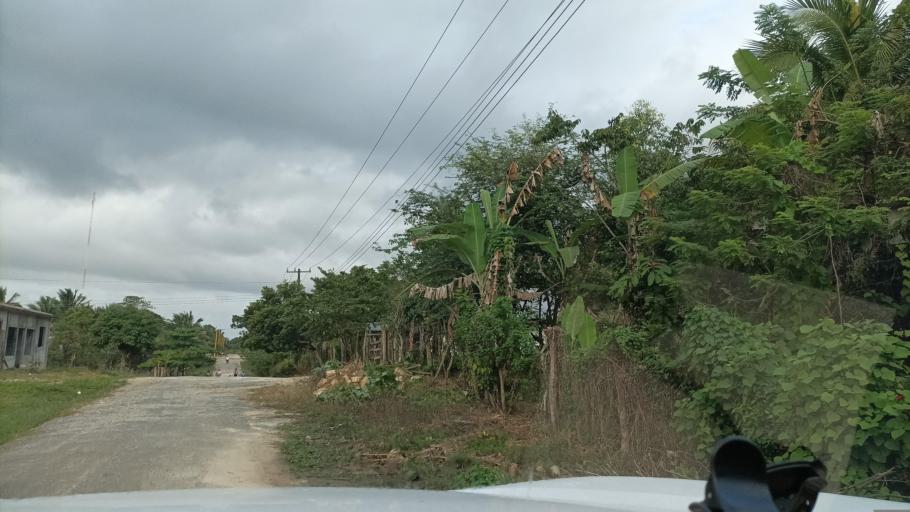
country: MX
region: Veracruz
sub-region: Moloacan
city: Cuichapa
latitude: 17.9232
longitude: -94.3666
